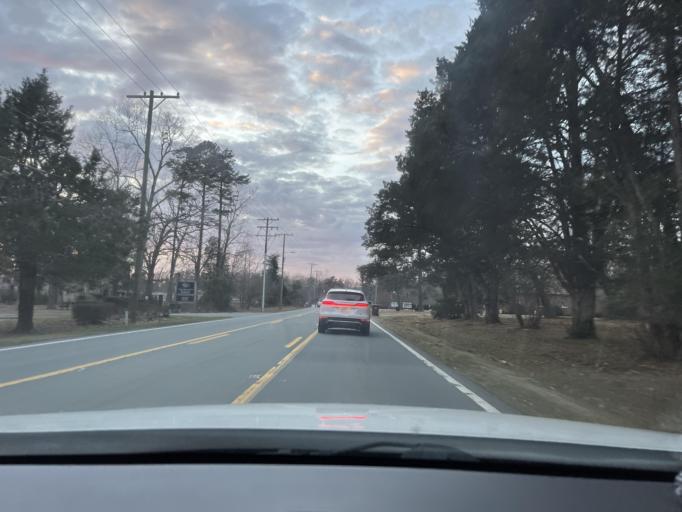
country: US
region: North Carolina
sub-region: Guilford County
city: McLeansville
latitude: 36.0683
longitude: -79.6246
